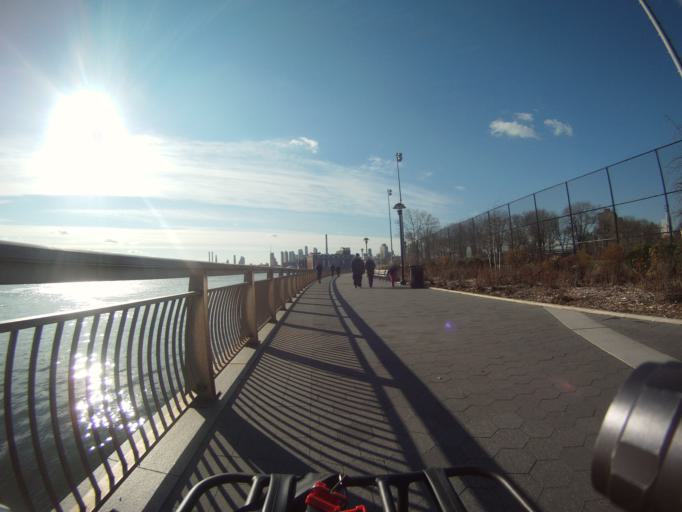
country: US
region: New York
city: New York City
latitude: 40.7122
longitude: -73.9764
